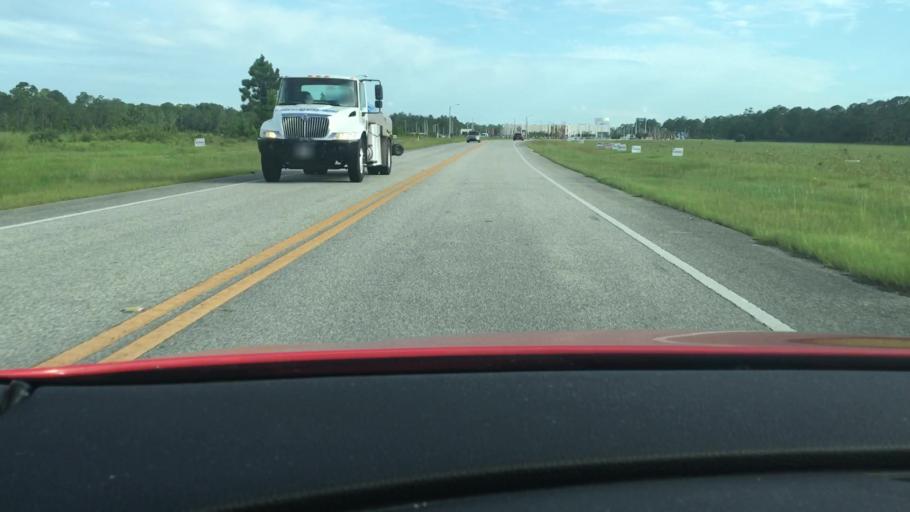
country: US
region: Florida
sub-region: Volusia County
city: Daytona Beach
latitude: 29.1843
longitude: -81.0930
